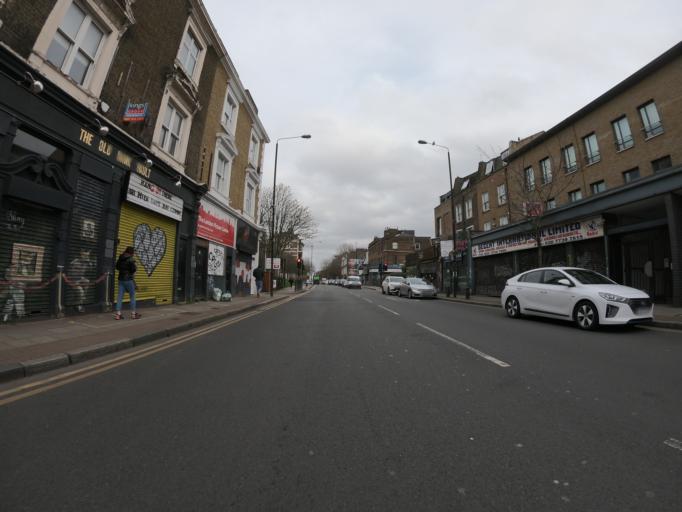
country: GB
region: England
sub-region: Greater London
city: Bethnal Green
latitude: 51.5311
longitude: -0.0679
